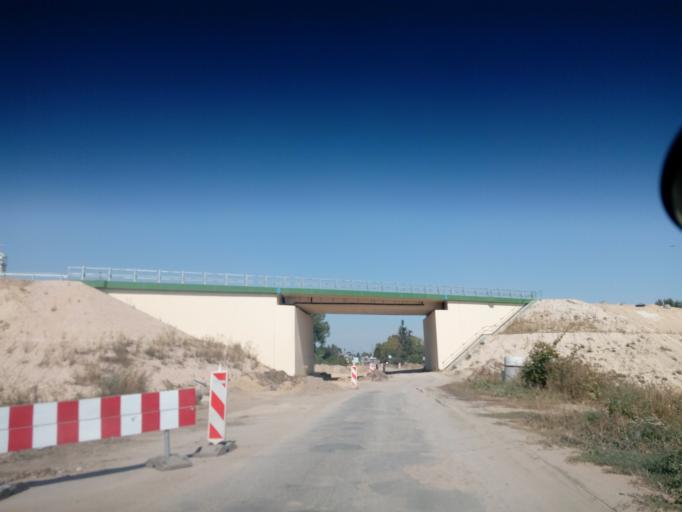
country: PL
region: Lublin Voivodeship
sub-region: Powiat hrubieszowski
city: Hrubieszow
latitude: 50.7886
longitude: 23.9013
